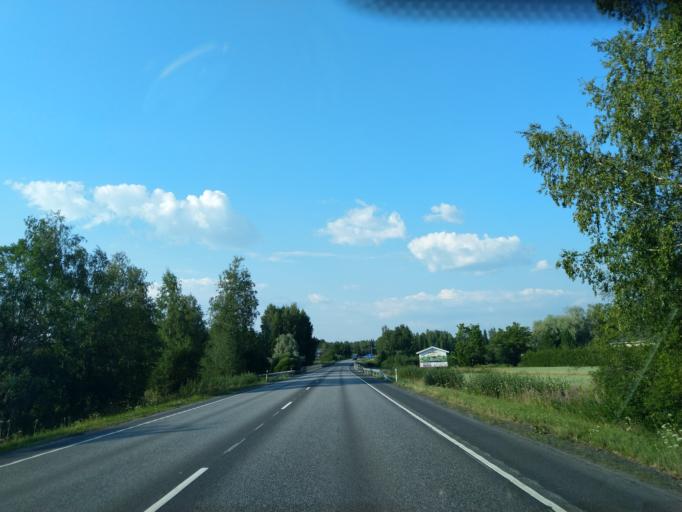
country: FI
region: Satakunta
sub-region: Pori
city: Pomarkku
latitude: 61.6950
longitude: 22.0044
